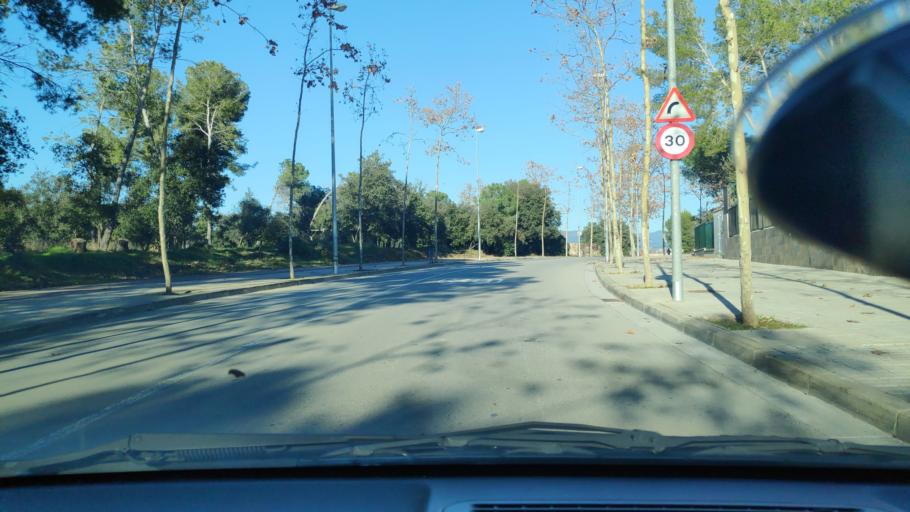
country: ES
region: Catalonia
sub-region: Provincia de Barcelona
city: Sant Quirze del Valles
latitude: 41.5628
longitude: 2.0741
